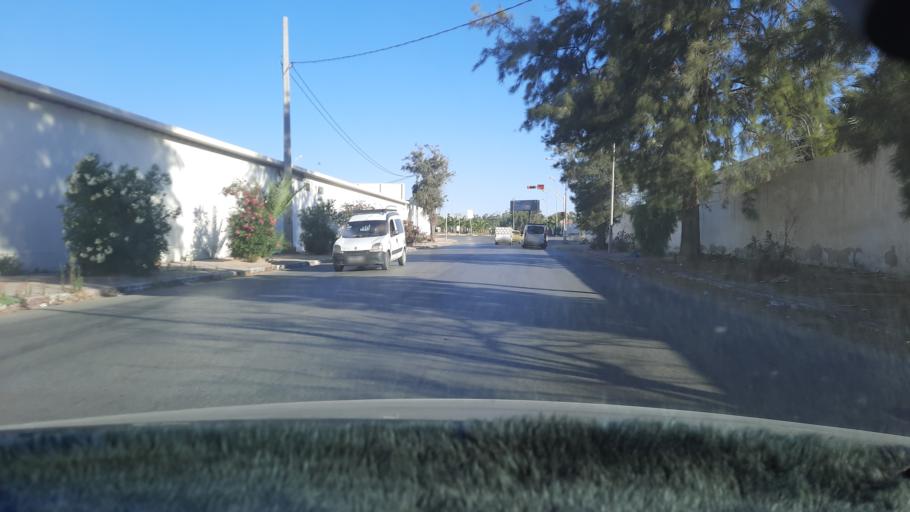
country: TN
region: Safaqis
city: Sfax
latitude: 34.7300
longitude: 10.7480
